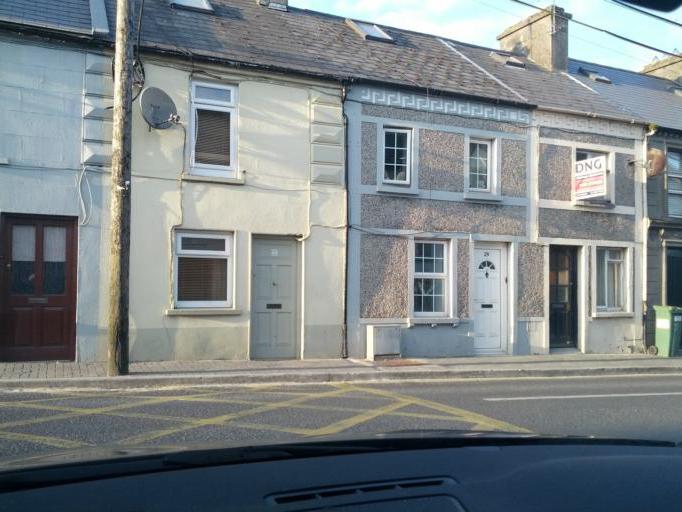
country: IE
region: Munster
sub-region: North Tipperary
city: Nenagh
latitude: 52.8634
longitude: -8.2026
